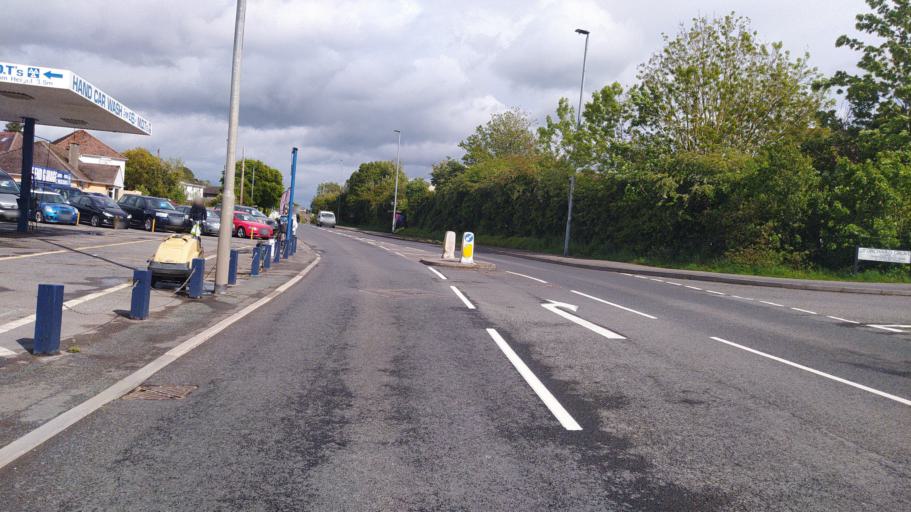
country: GB
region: England
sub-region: Devon
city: Newton Abbot
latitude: 50.5359
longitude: -3.6398
